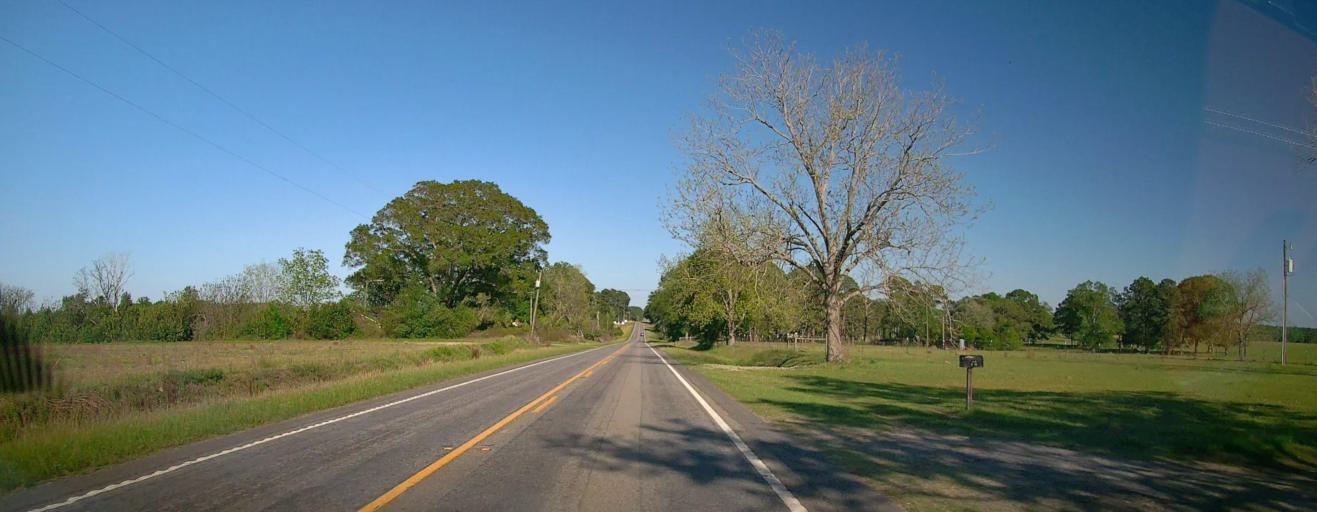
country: US
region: Georgia
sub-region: Ben Hill County
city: Fitzgerald
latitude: 31.7195
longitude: -83.3772
